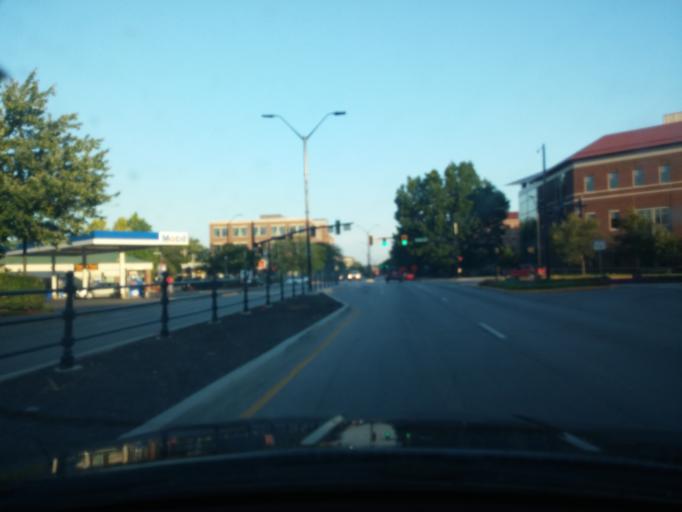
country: US
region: Indiana
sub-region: Tippecanoe County
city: West Lafayette
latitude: 40.4319
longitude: -86.9147
